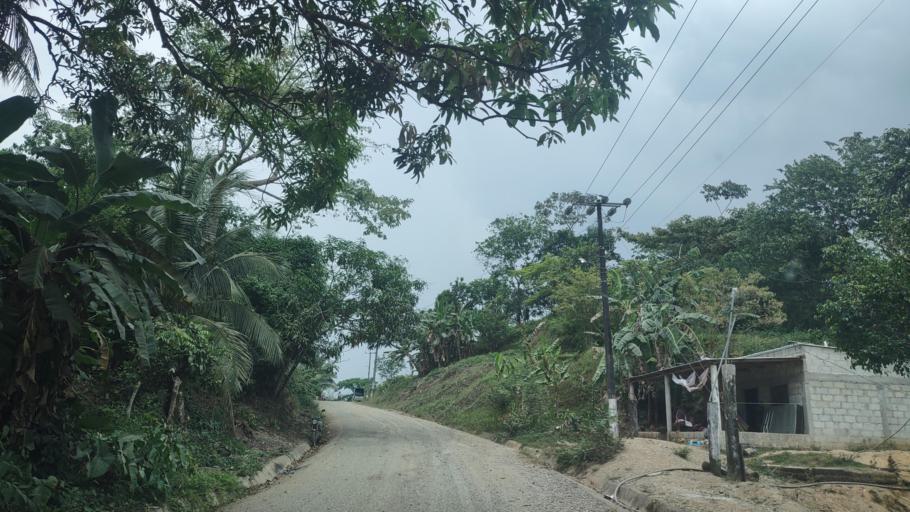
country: MX
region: Veracruz
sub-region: Uxpanapa
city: Poblado 10
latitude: 17.4532
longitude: -94.0992
